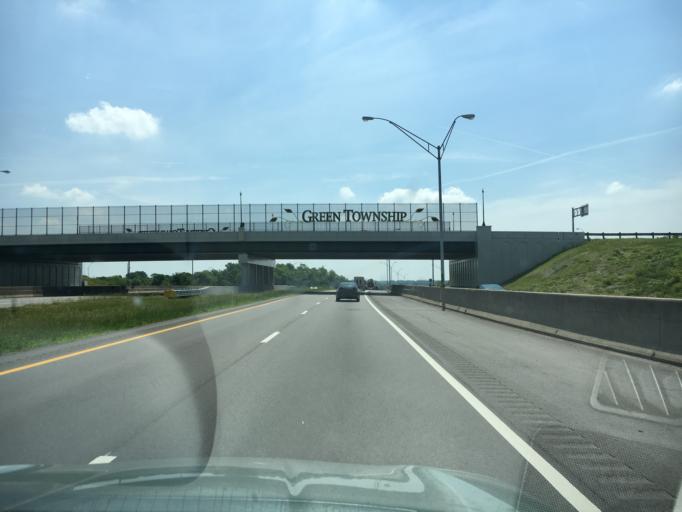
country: US
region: Ohio
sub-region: Hamilton County
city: Monfort Heights
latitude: 39.1851
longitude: -84.6050
